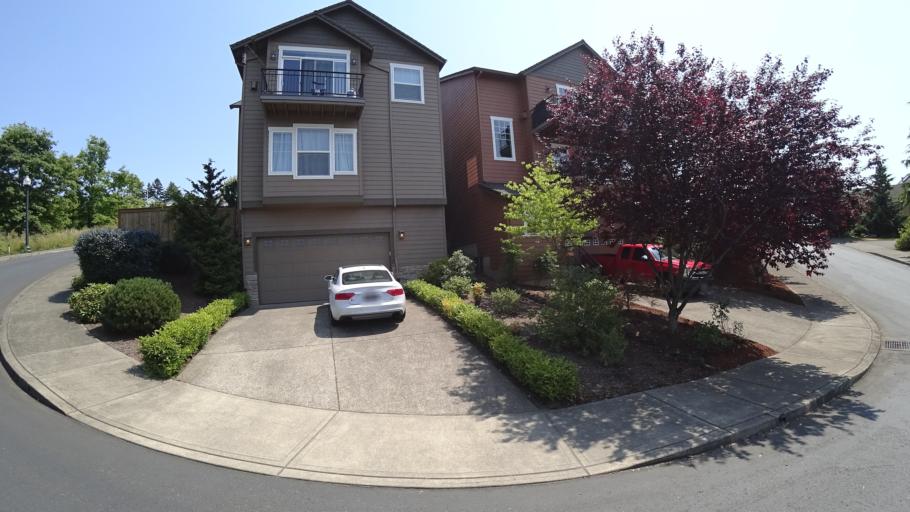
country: US
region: Oregon
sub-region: Multnomah County
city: Lents
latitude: 45.4554
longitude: -122.5671
